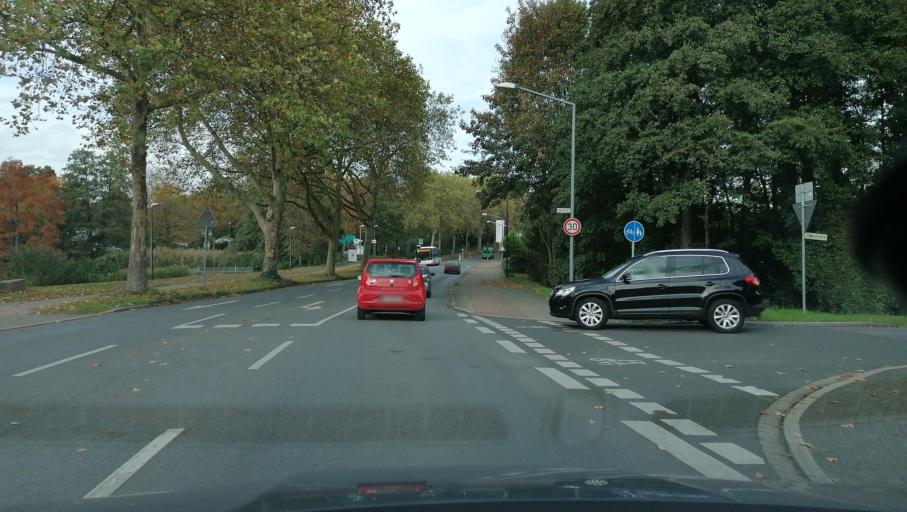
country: DE
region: North Rhine-Westphalia
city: Herten
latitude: 51.6012
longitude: 7.1413
